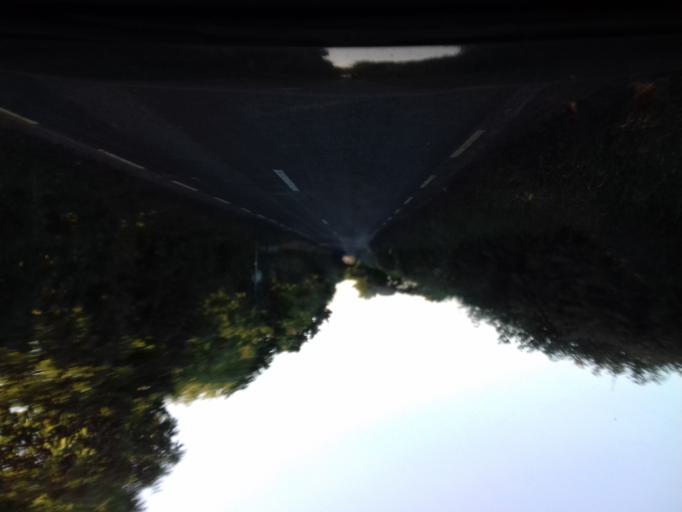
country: IE
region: Leinster
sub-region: Dublin City
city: Finglas
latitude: 53.4477
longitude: -6.3339
